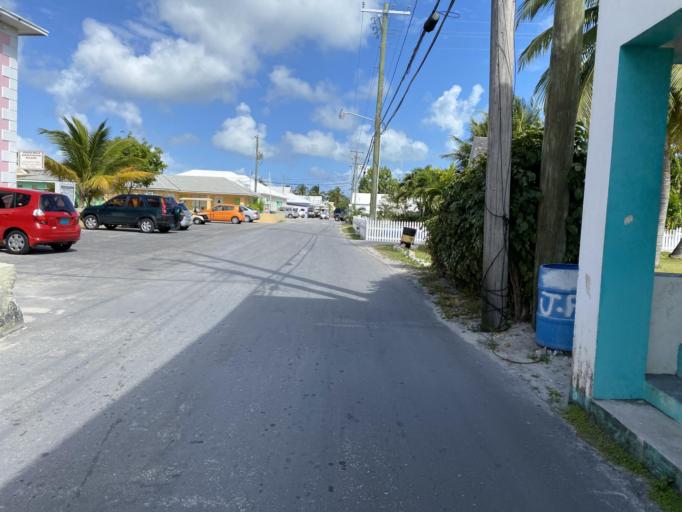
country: BS
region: Spanish Wells
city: Spanish Wells
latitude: 25.5437
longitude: -76.7493
